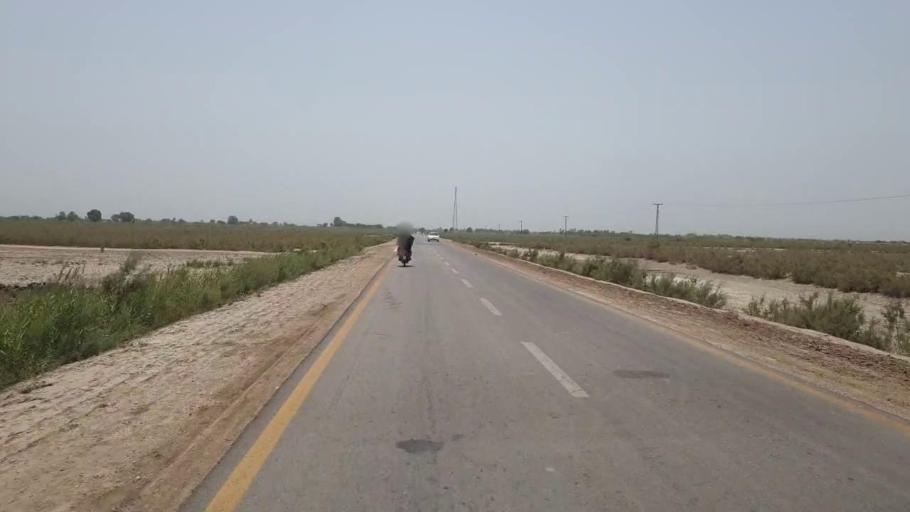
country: PK
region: Sindh
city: Moro
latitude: 26.6014
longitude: 68.0726
